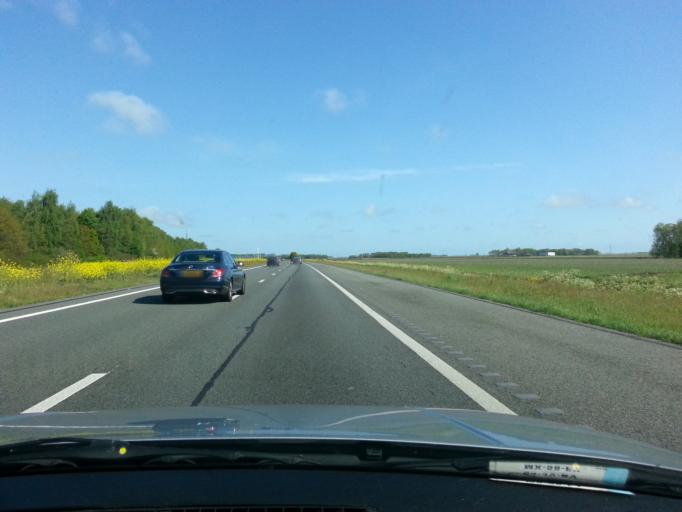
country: NL
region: Friesland
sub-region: Gemeente Lemsterland
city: Lemmer
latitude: 52.8105
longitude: 5.7471
